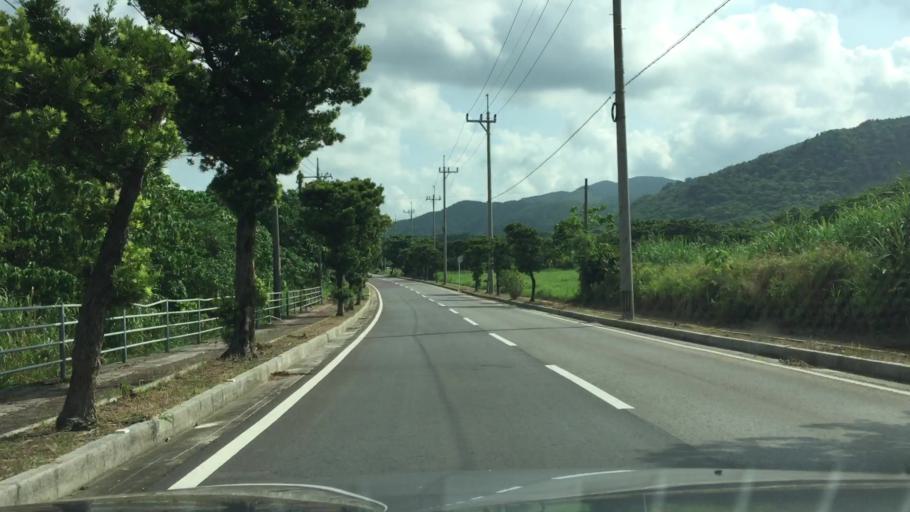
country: JP
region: Okinawa
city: Ishigaki
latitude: 24.4691
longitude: 124.2516
